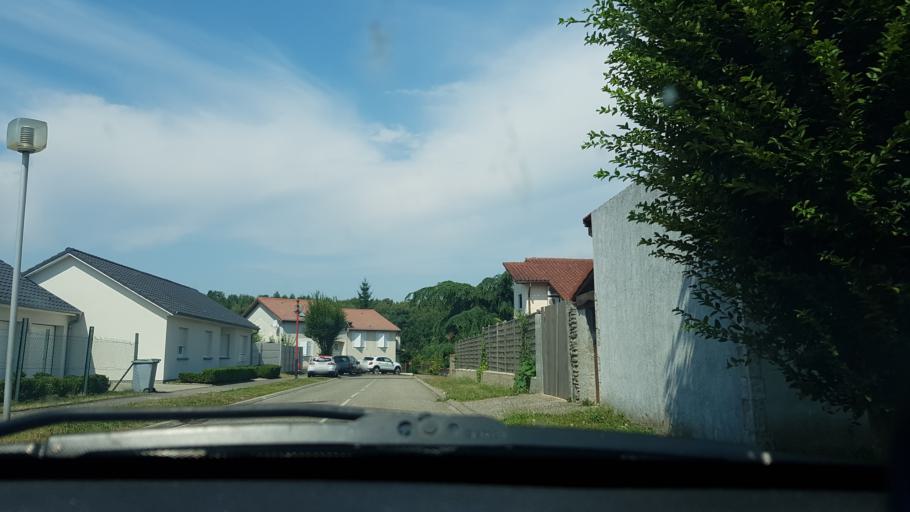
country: FR
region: Lorraine
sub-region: Departement de la Moselle
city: Porcelette
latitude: 49.1615
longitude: 6.6563
